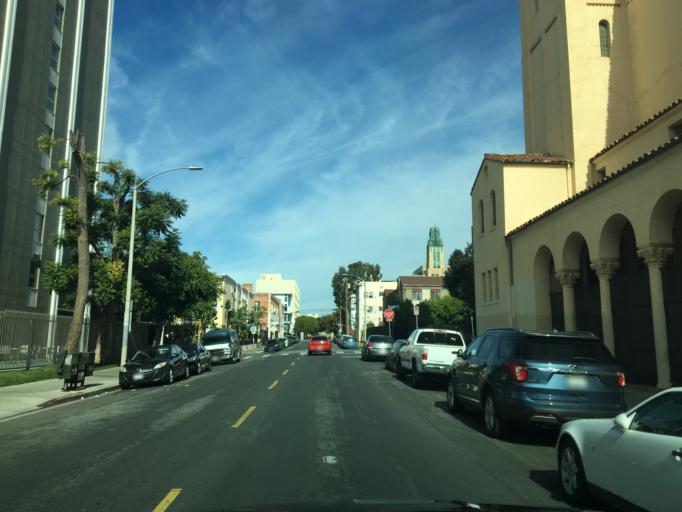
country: US
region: California
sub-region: Los Angeles County
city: Silver Lake
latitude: 34.0582
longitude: -118.2891
